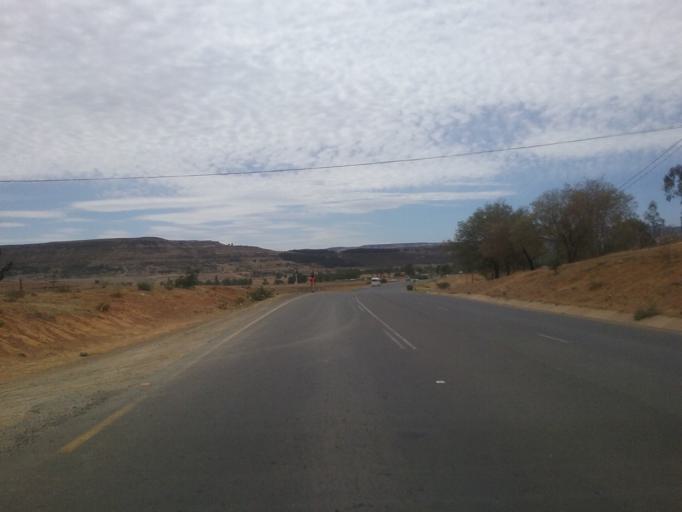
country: LS
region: Maseru
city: Nako
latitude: -29.6267
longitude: 27.4880
